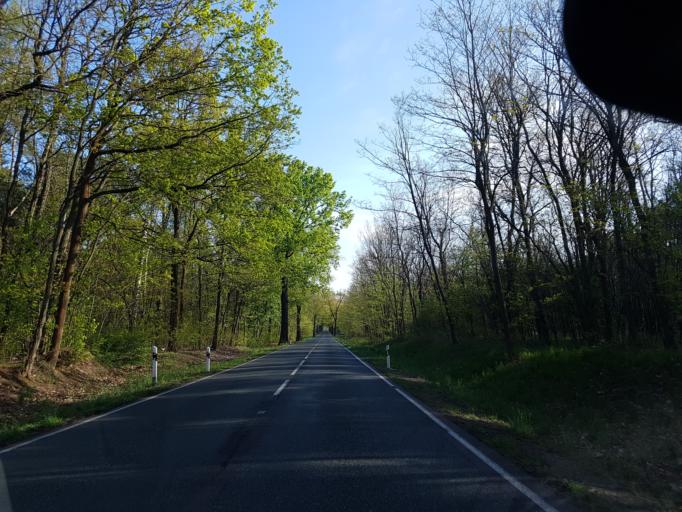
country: DE
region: Brandenburg
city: Altdobern
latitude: 51.6323
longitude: 14.0299
